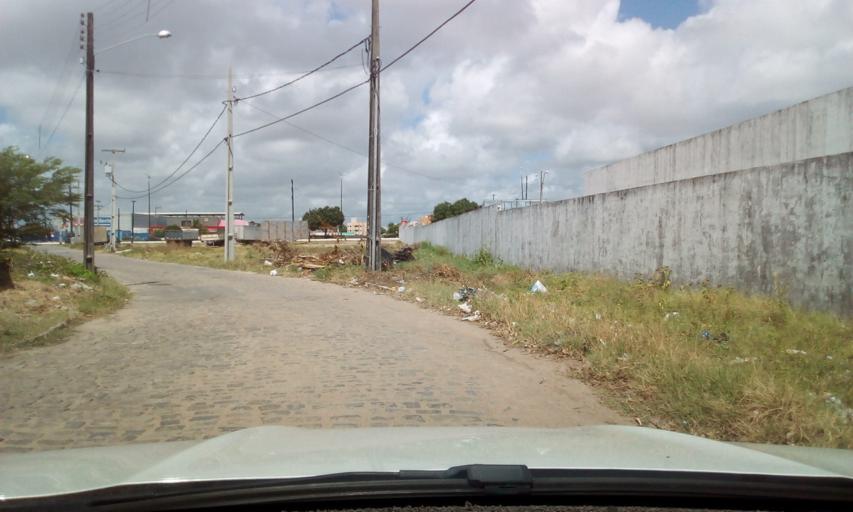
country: BR
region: Paraiba
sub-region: Joao Pessoa
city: Joao Pessoa
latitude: -7.1667
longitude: -34.8510
